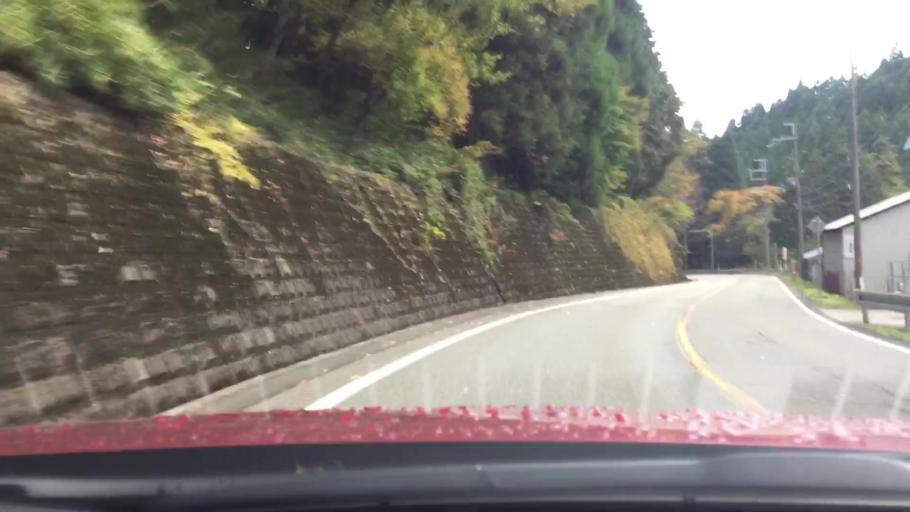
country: JP
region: Hyogo
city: Yamazakicho-nakabirose
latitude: 35.1814
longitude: 134.5356
